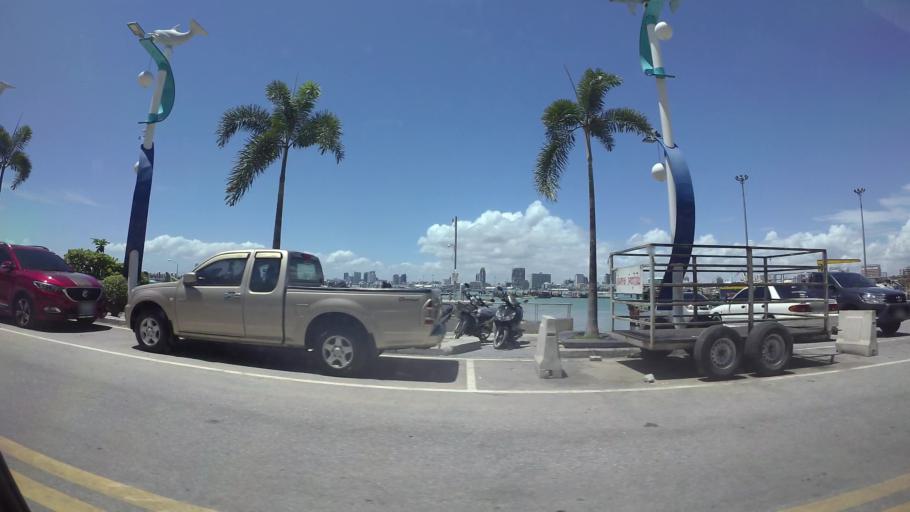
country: TH
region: Chon Buri
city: Phatthaya
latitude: 12.9276
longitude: 100.8640
